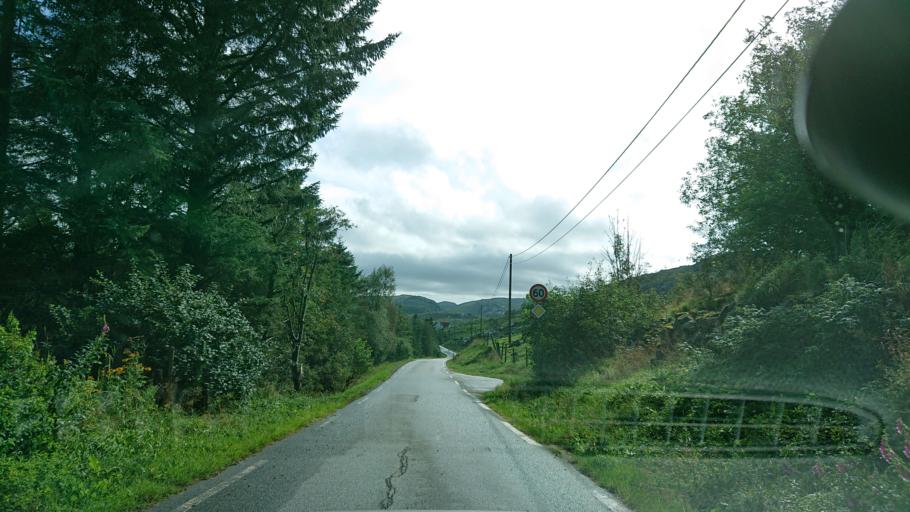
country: NO
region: Rogaland
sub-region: Gjesdal
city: Algard
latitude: 58.7009
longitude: 5.8905
